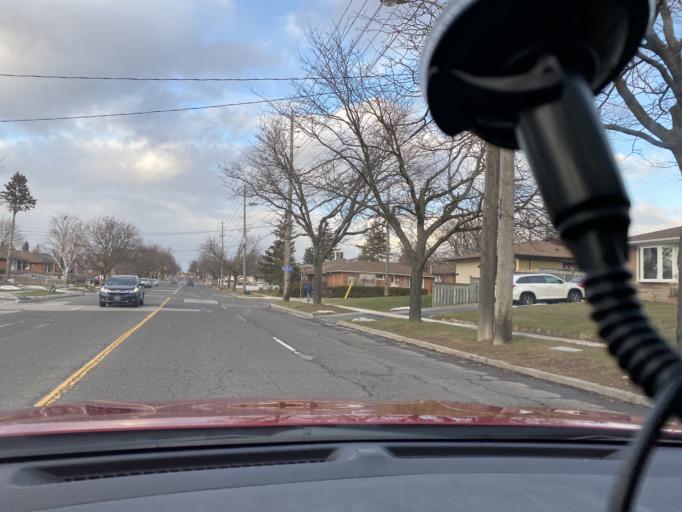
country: CA
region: Ontario
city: Scarborough
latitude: 43.7713
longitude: -79.2192
